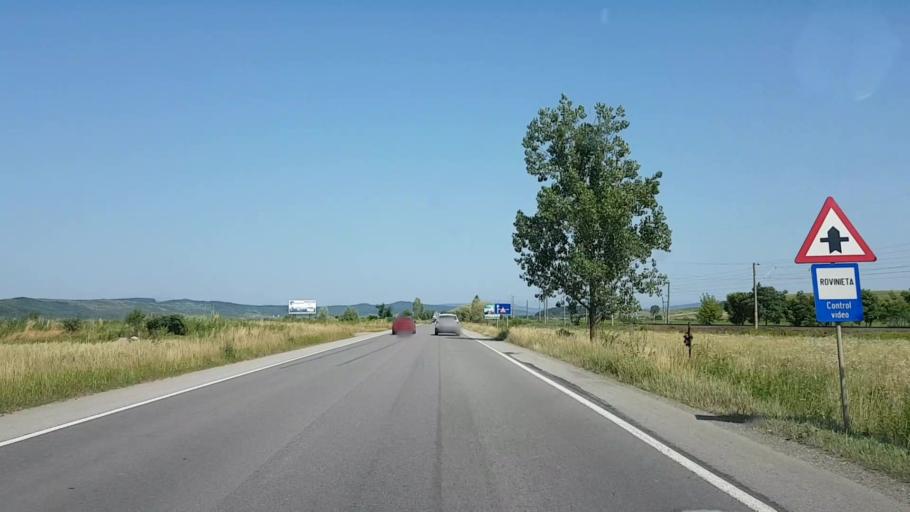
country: RO
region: Bistrita-Nasaud
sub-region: Comuna Sintereag
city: Cociu
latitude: 47.1838
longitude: 24.2151
